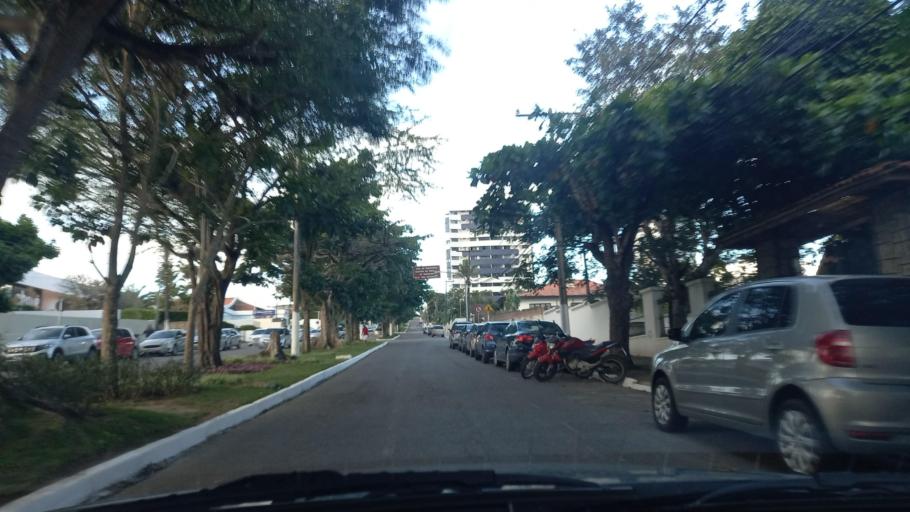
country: BR
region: Pernambuco
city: Garanhuns
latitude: -8.8816
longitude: -36.4761
